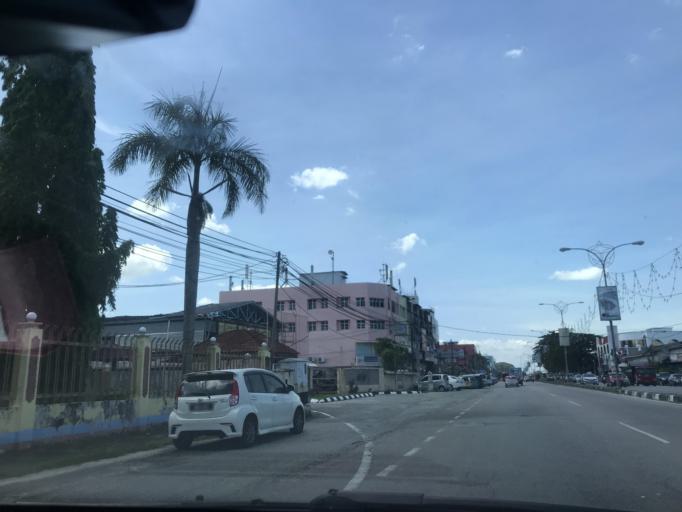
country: MY
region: Kelantan
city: Kota Bharu
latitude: 6.1056
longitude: 102.2596
